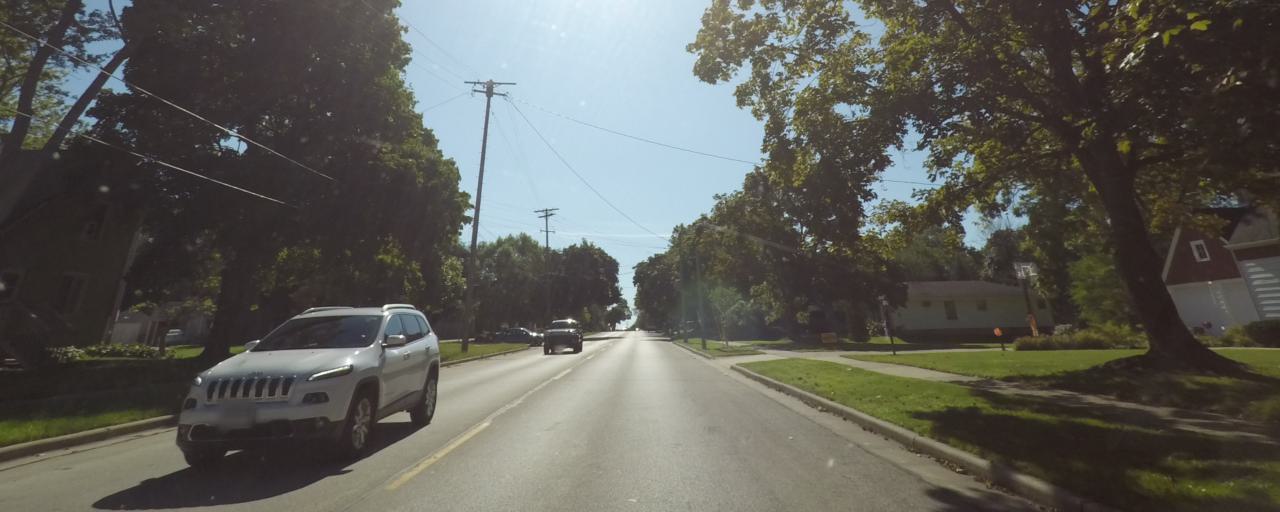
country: US
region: Wisconsin
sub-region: Waukesha County
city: Waukesha
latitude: 43.0016
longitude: -88.2148
